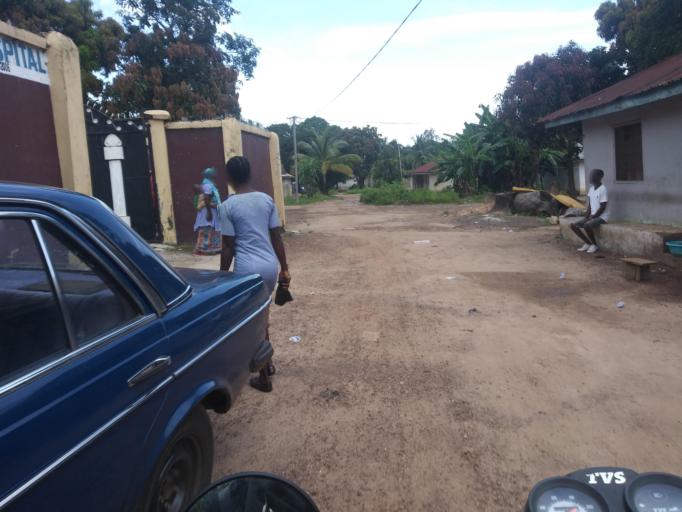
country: SL
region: Northern Province
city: Makeni
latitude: 8.8726
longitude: -12.0410
